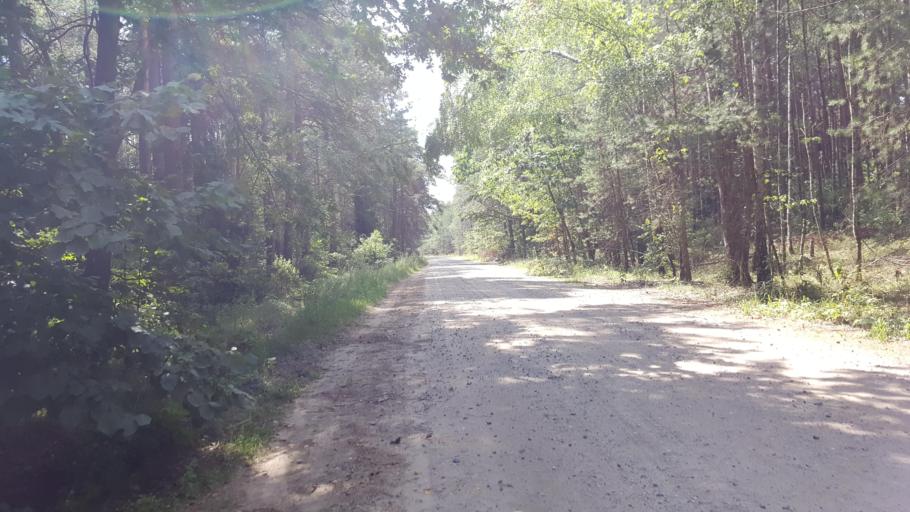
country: PL
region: Podlasie
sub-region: Powiat hajnowski
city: Hajnowka
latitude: 52.5636
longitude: 23.5555
